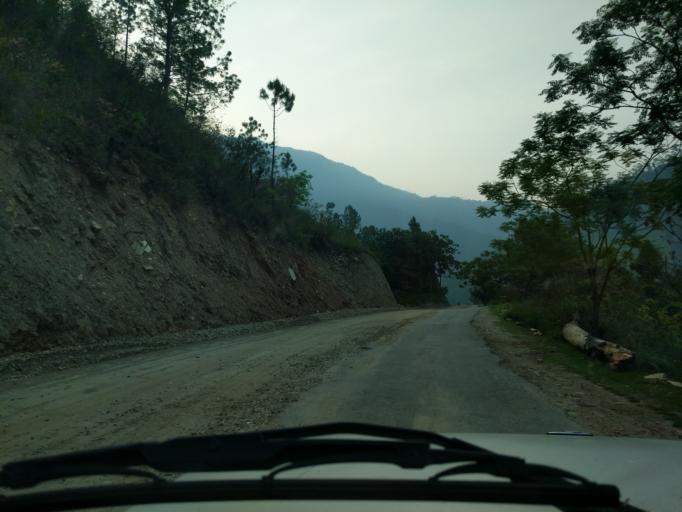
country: BT
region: Mongar
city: Mongar
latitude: 27.2616
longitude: 91.1789
